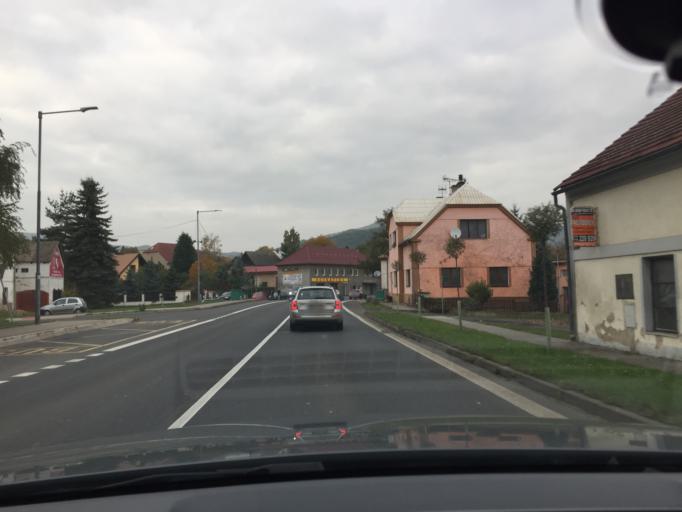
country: CZ
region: Ustecky
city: Velemin
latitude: 50.5381
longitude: 13.9776
